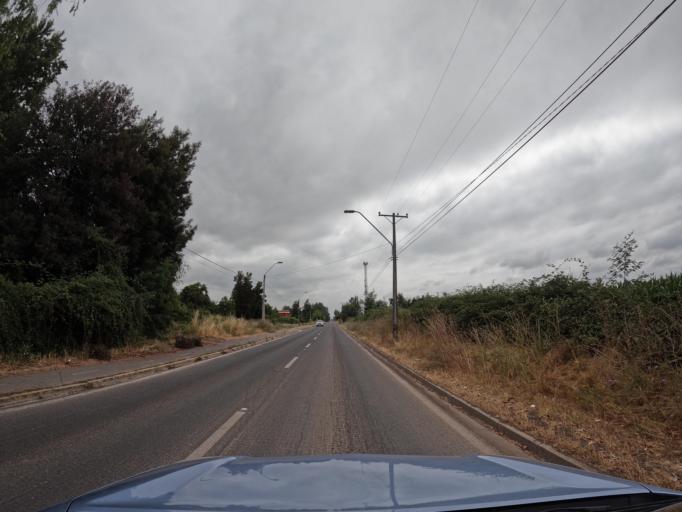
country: CL
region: O'Higgins
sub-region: Provincia de Colchagua
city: Chimbarongo
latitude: -34.7241
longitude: -71.0550
